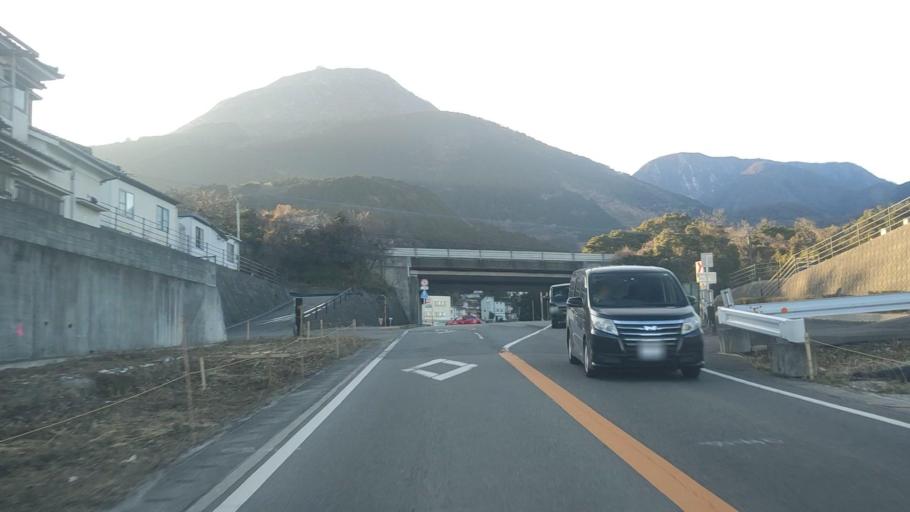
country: JP
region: Oita
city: Beppu
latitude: 33.2876
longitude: 131.4653
